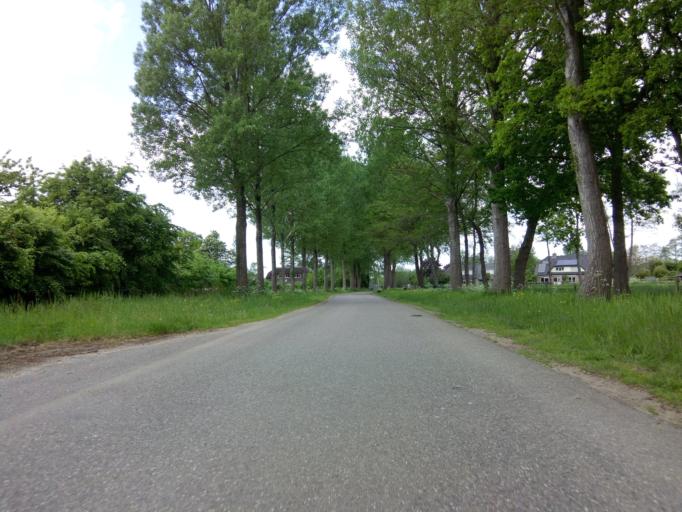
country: NL
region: Gelderland
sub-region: Gemeente Ede
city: Lunteren
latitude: 52.0593
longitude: 5.6329
